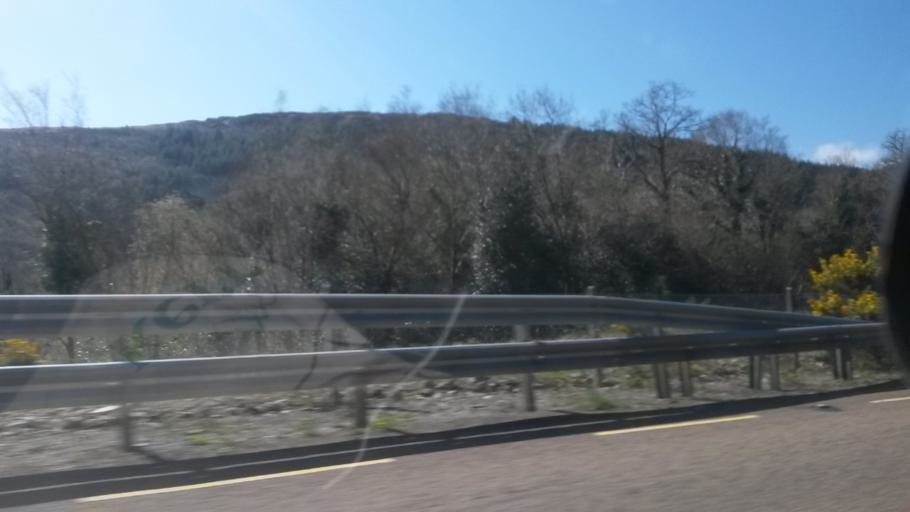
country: IE
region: Munster
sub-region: Ciarrai
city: Cill Airne
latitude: 51.9628
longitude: -9.3621
